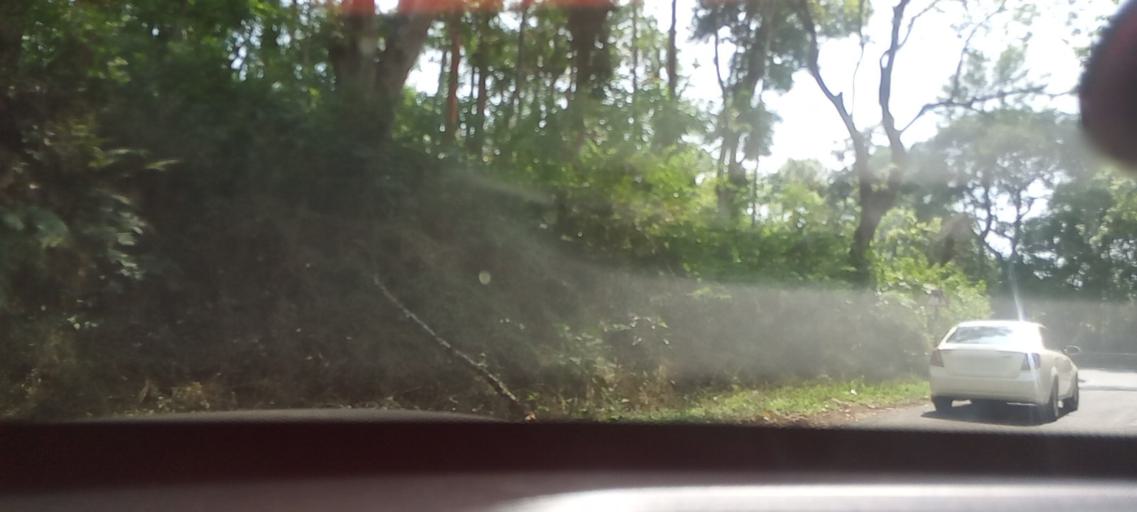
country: IN
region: Karnataka
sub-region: Chikmagalur
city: Mudigere
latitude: 13.2663
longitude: 75.6247
